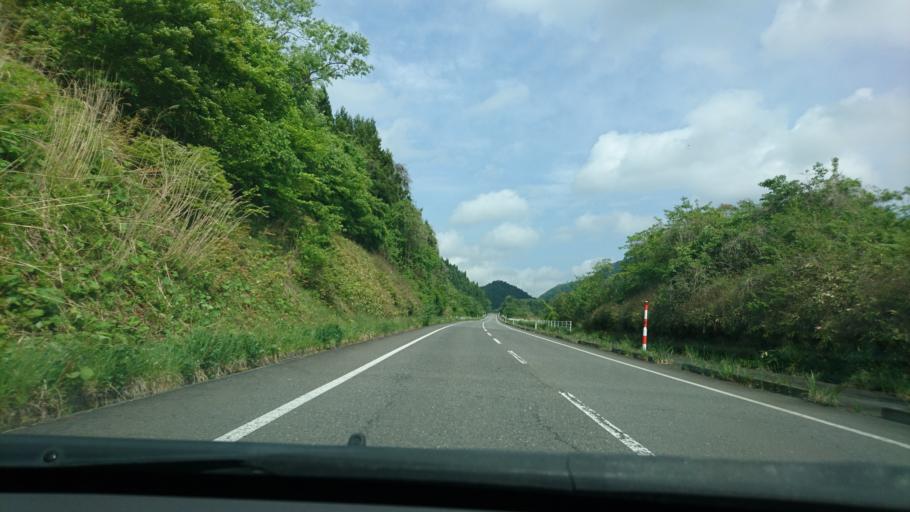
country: JP
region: Iwate
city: Ichinoseki
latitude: 38.8953
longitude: 140.9346
